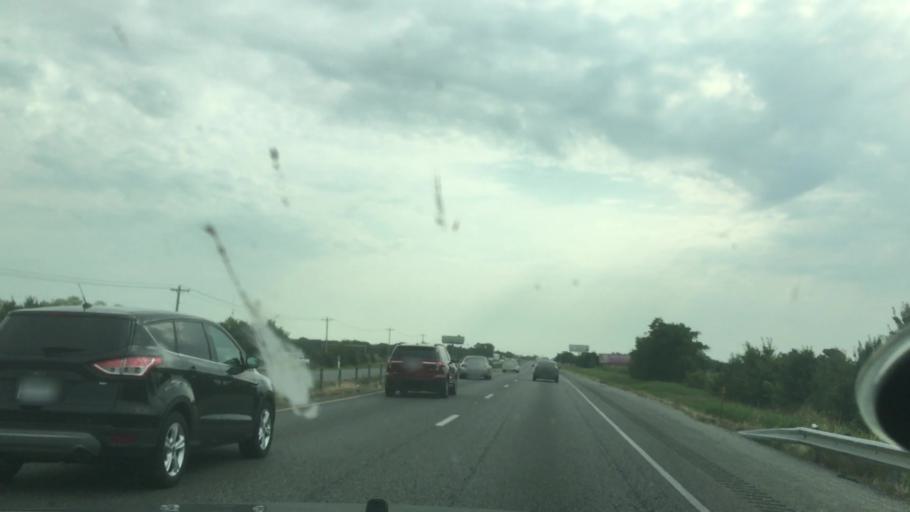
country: US
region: Oklahoma
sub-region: Bryan County
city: Colbert
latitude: 33.8850
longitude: -96.4905
